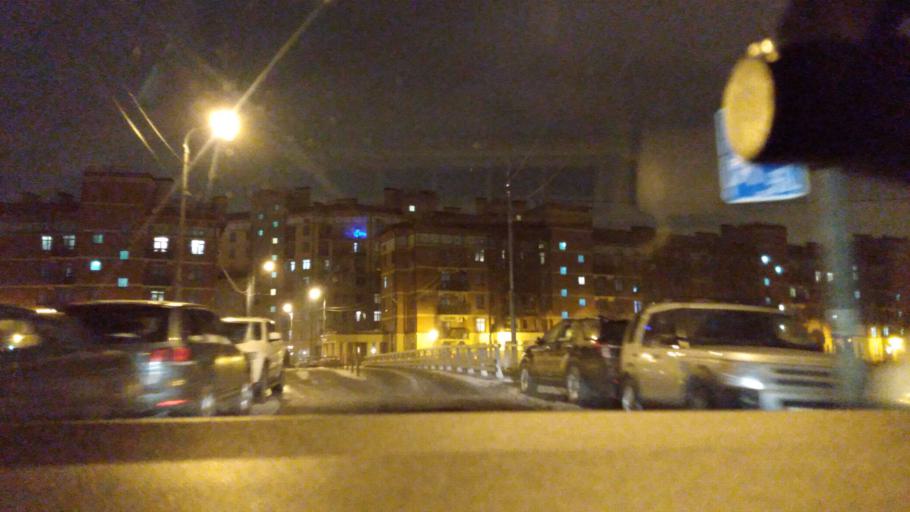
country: RU
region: Moskovskaya
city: Sheremet'yevskiy
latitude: 55.9605
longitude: 37.4397
